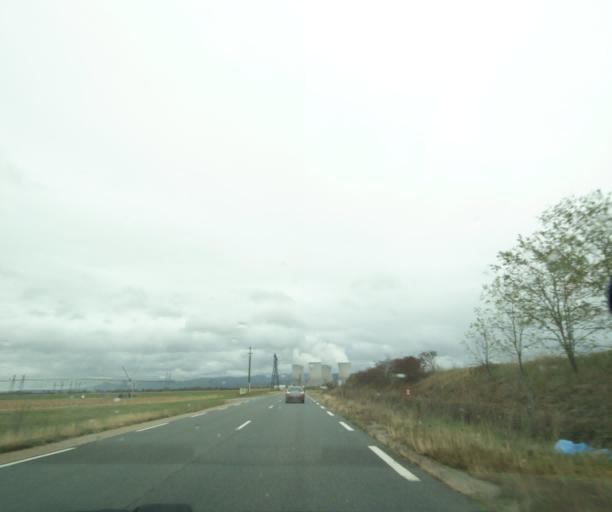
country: FR
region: Rhone-Alpes
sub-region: Departement de l'Ain
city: Loyettes
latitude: 45.7939
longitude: 5.2483
